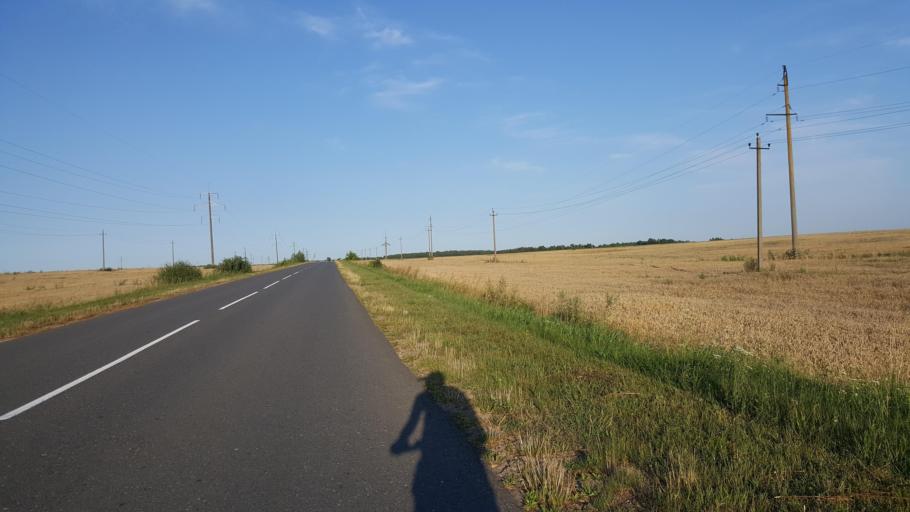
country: BY
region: Brest
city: Kamyanyets
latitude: 52.3792
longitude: 23.6581
